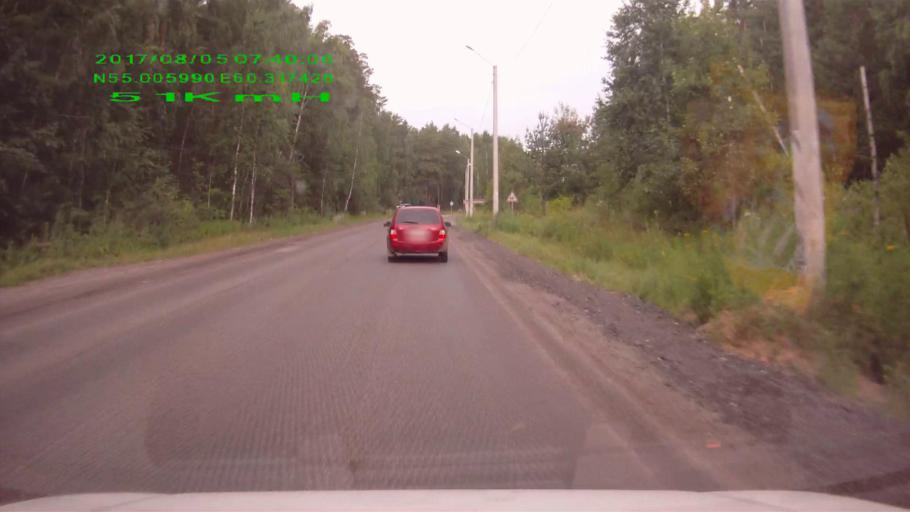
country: RU
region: Chelyabinsk
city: Chebarkul'
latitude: 55.0060
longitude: 60.3171
